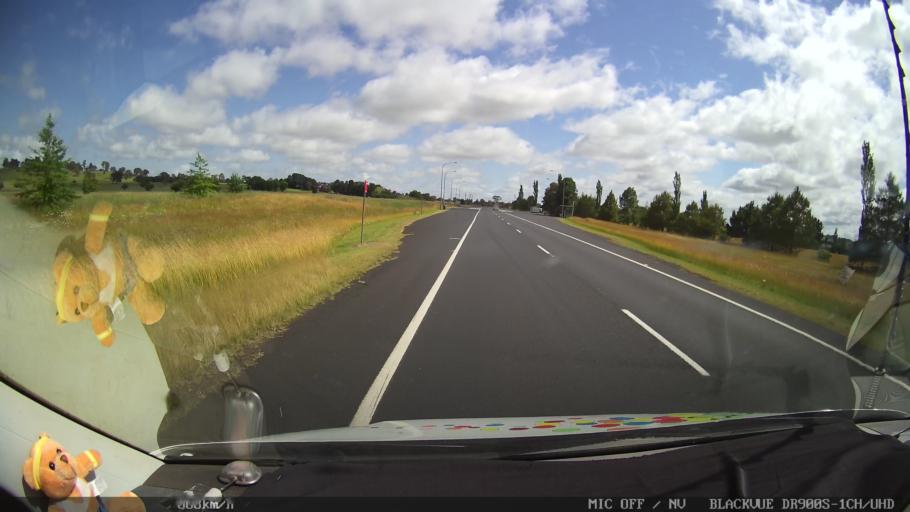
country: AU
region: New South Wales
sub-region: Glen Innes Severn
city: Glen Innes
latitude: -29.9243
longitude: 151.7241
